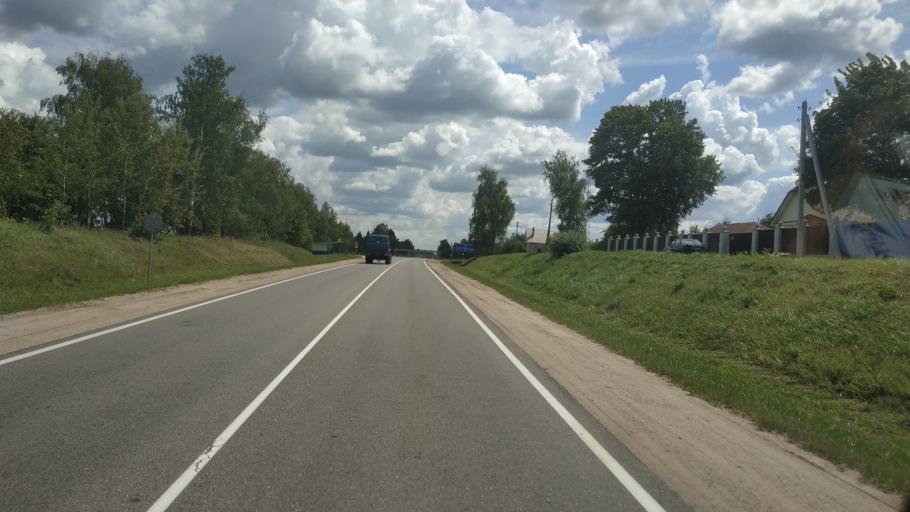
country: BY
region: Mogilev
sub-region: Mahilyowski Rayon
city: Veyno
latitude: 53.8156
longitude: 30.4490
